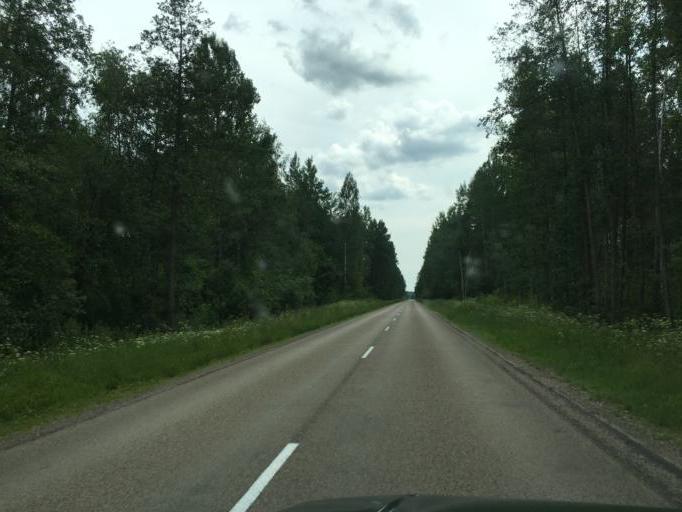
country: LV
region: Rugaju
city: Rugaji
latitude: 56.8200
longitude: 27.0949
